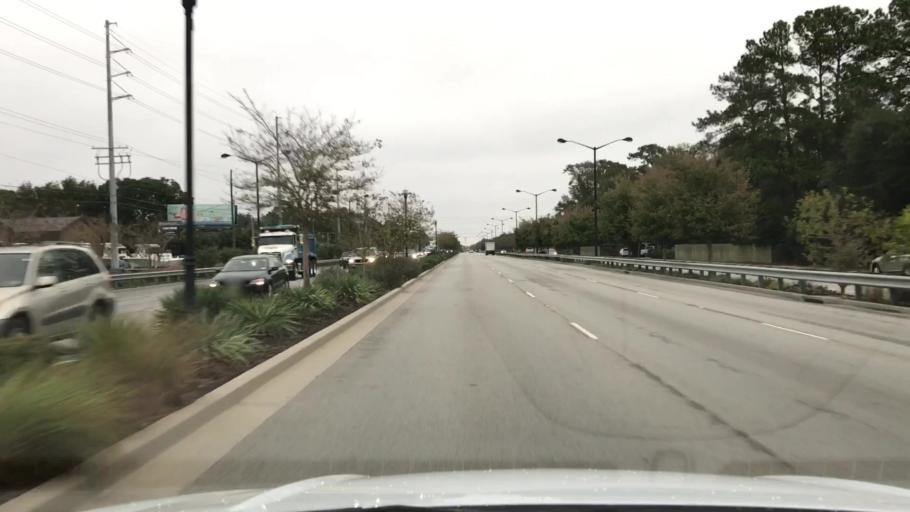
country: US
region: South Carolina
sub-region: Charleston County
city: Mount Pleasant
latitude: 32.8058
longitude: -79.8868
